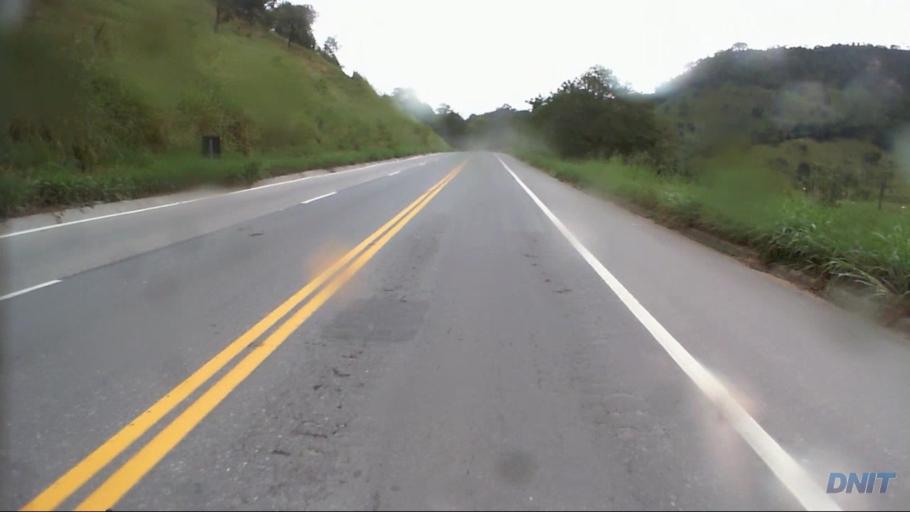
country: BR
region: Minas Gerais
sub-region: Nova Era
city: Nova Era
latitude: -19.7067
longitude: -42.9992
